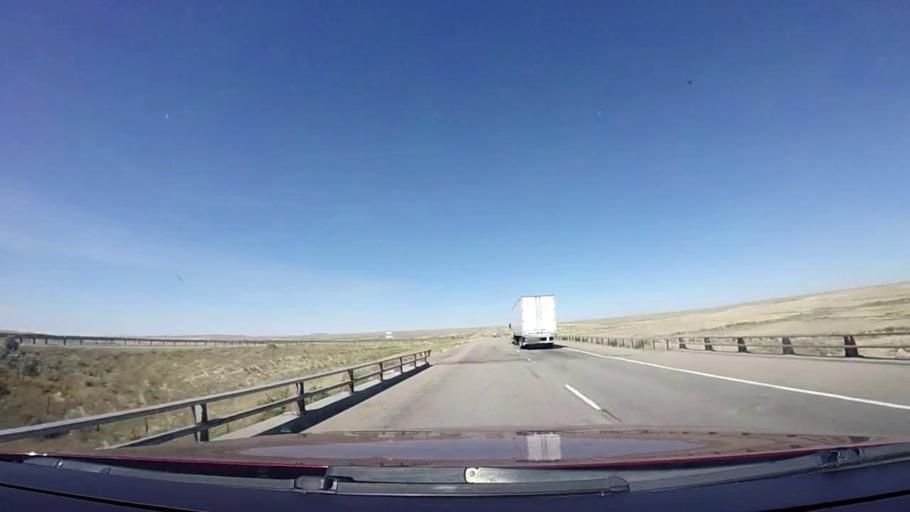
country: US
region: Wyoming
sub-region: Sweetwater County
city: Rock Springs
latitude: 41.6405
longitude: -108.4911
